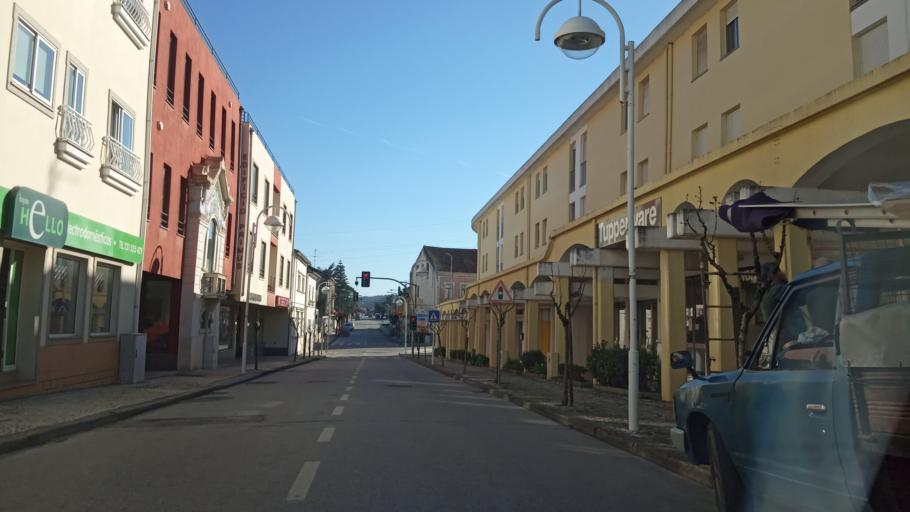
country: PT
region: Aveiro
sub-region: Anadia
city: Anadia
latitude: 40.4407
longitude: -8.4363
